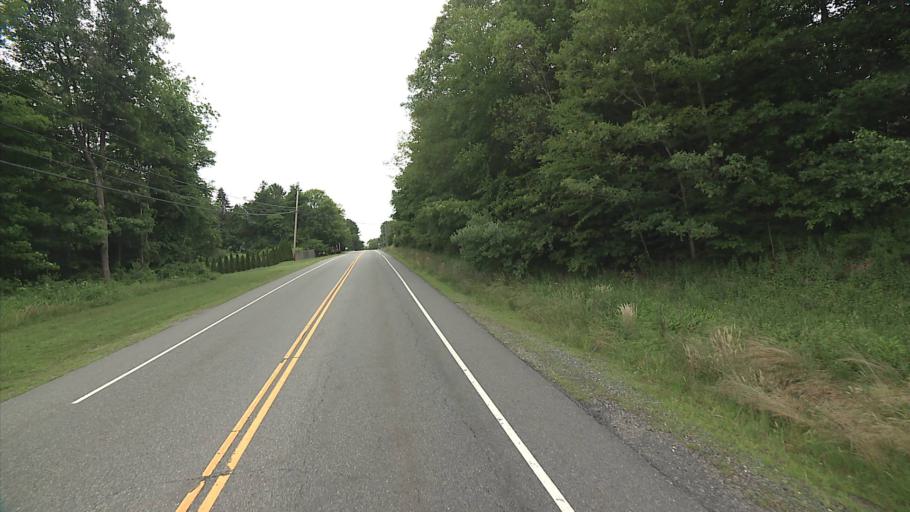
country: US
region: Connecticut
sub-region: New London County
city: Ledyard Center
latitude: 41.4238
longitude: -72.0165
